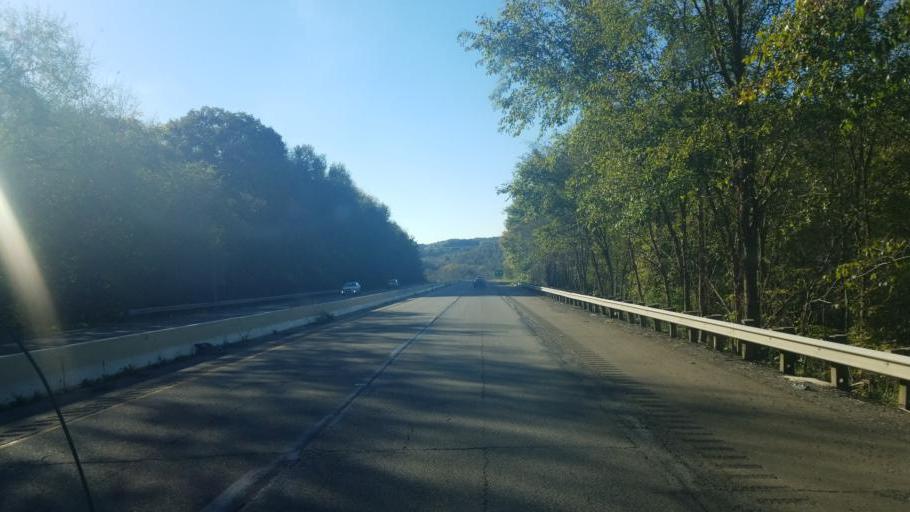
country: US
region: Ohio
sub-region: Columbiana County
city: Glenmoor
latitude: 40.6740
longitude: -80.6137
